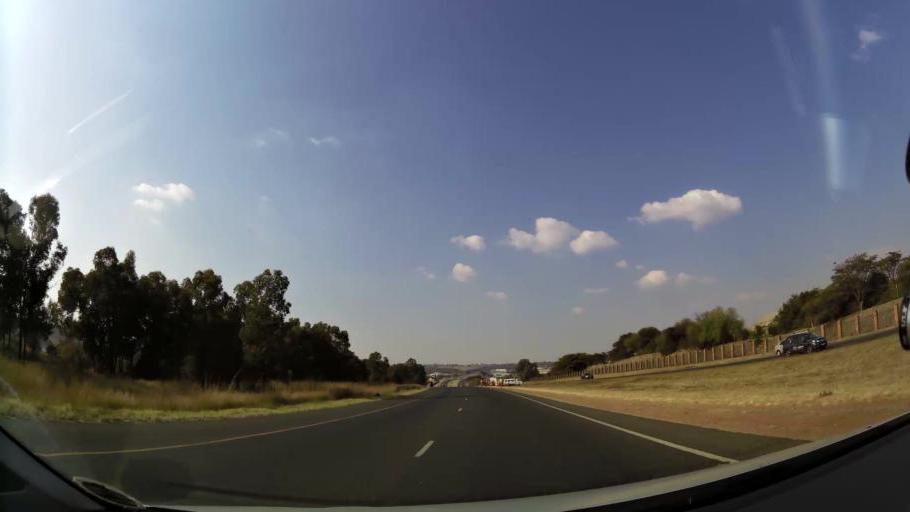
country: ZA
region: Gauteng
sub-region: City of Johannesburg Metropolitan Municipality
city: Modderfontein
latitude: -26.1088
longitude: 28.1634
